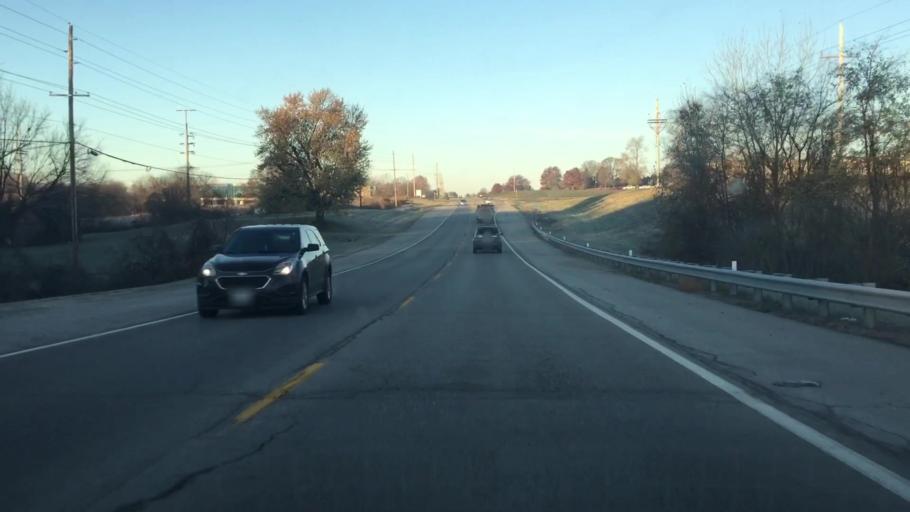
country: US
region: Missouri
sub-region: Buchanan County
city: Saint Joseph
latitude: 39.7555
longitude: -94.7737
